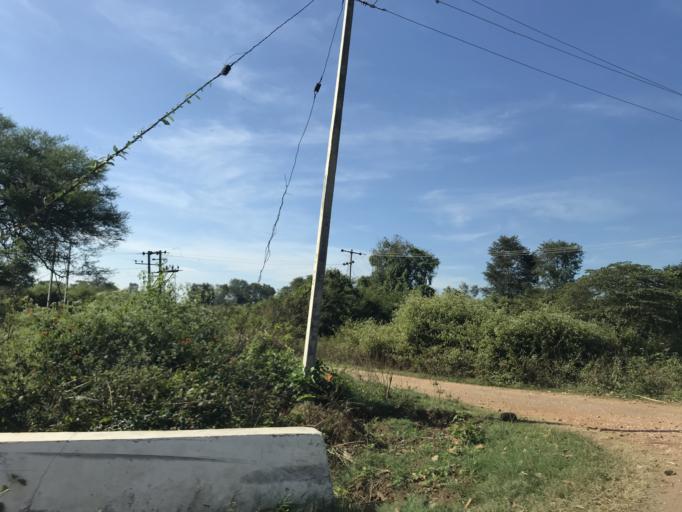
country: IN
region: Karnataka
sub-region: Mysore
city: Sargur
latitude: 12.1214
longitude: 76.4849
